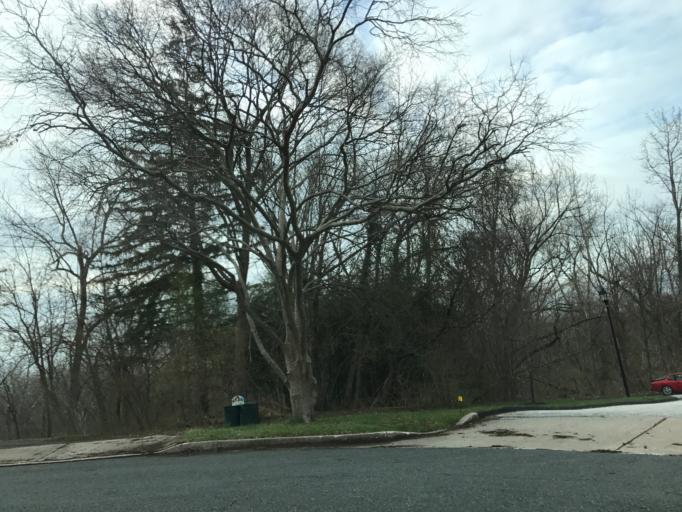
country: US
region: Maryland
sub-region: Baltimore County
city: Lutherville
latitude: 39.4164
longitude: -76.6362
